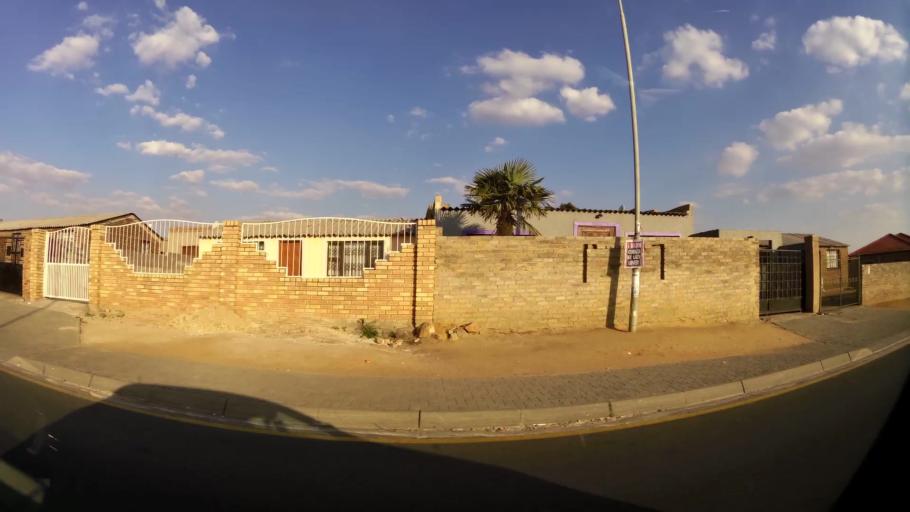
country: ZA
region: Gauteng
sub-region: City of Johannesburg Metropolitan Municipality
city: Roodepoort
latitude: -26.2128
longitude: 27.8919
